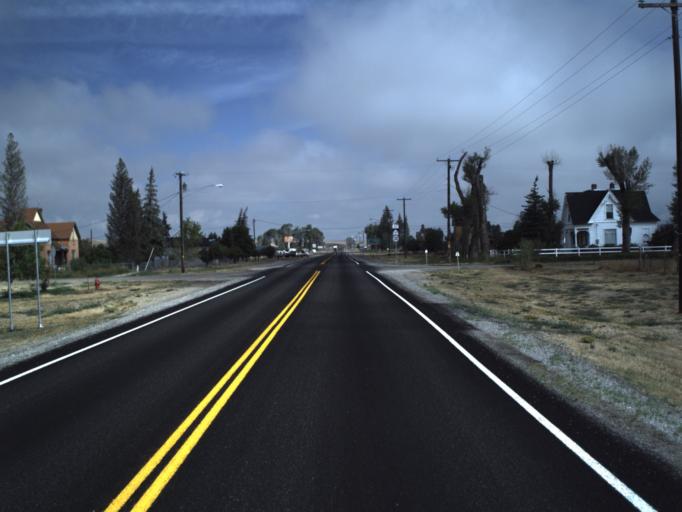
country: US
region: Utah
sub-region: Rich County
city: Randolph
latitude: 41.5211
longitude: -111.1629
